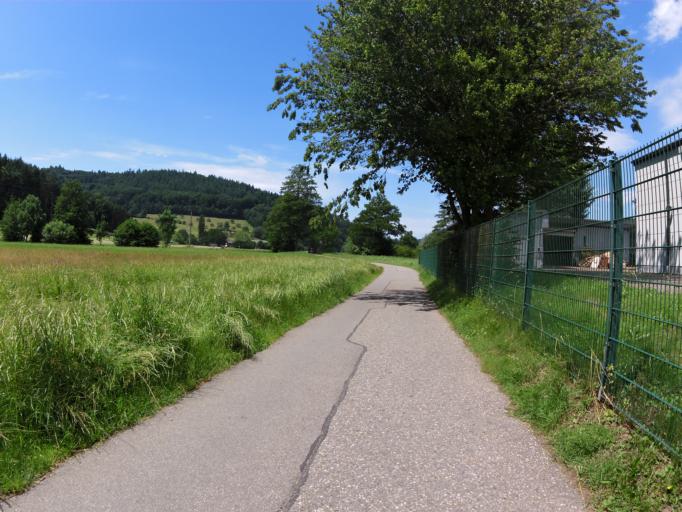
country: DE
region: Baden-Wuerttemberg
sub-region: Freiburg Region
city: Seelbach
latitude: 48.3256
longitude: 7.9292
